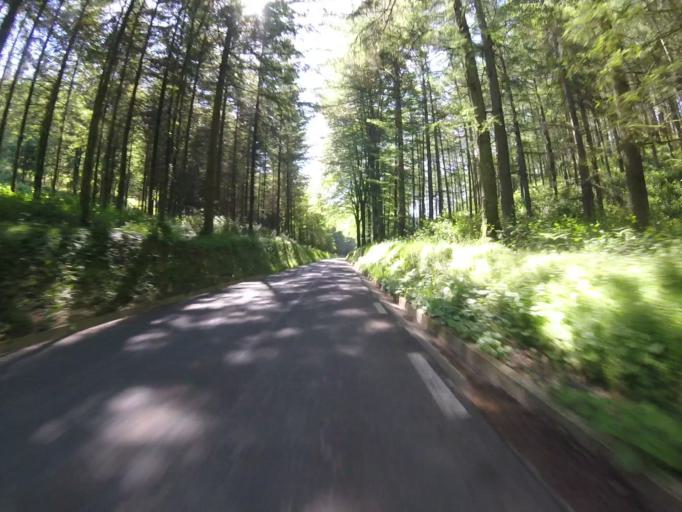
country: ES
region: Basque Country
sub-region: Provincia de Guipuzcoa
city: Albiztur
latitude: 43.1220
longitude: -2.1640
